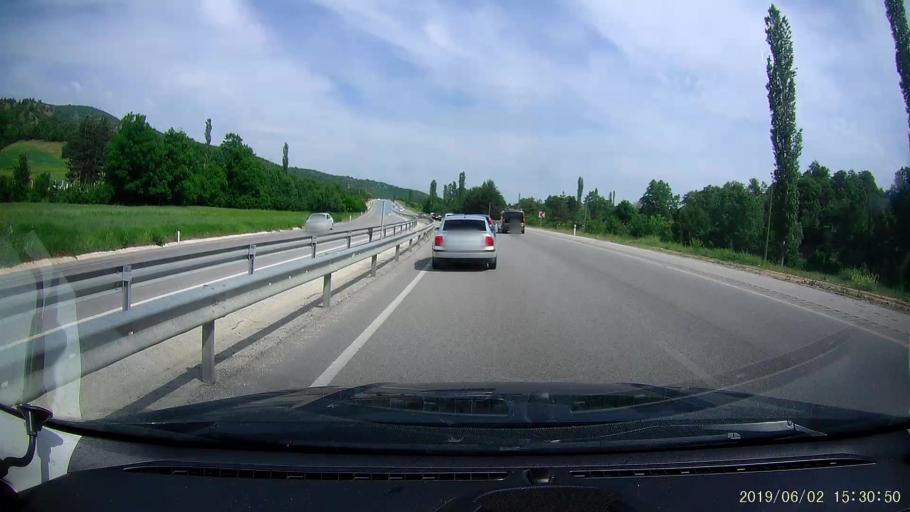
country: TR
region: Amasya
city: Saraycik
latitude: 40.9491
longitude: 35.1160
